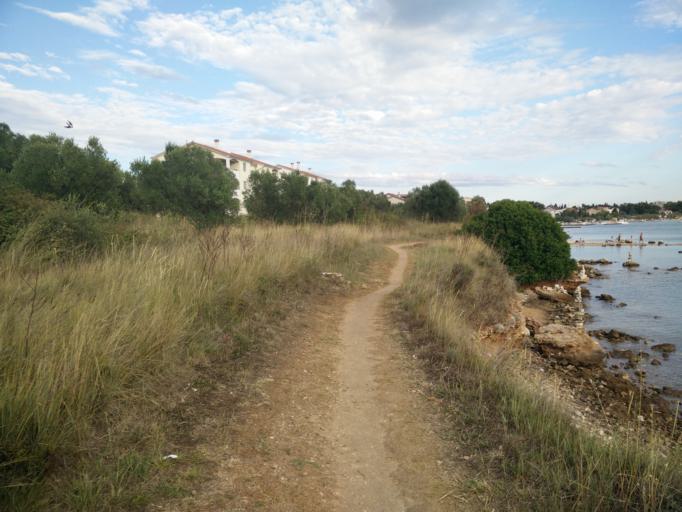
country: HR
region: Zadarska
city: Biograd na Moru
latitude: 43.9498
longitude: 15.4411
